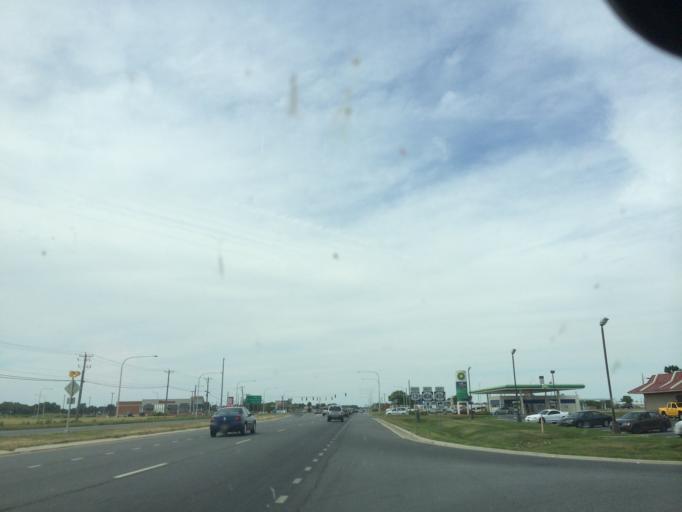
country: US
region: Delaware
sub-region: Sussex County
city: Bridgeville
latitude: 38.7211
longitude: -75.5898
